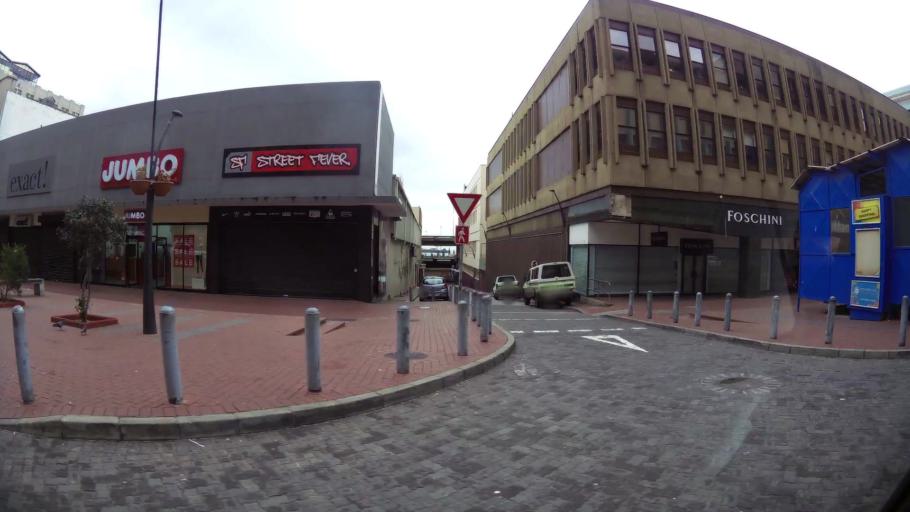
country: ZA
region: Eastern Cape
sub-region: Nelson Mandela Bay Metropolitan Municipality
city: Port Elizabeth
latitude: -33.9604
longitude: 25.6218
